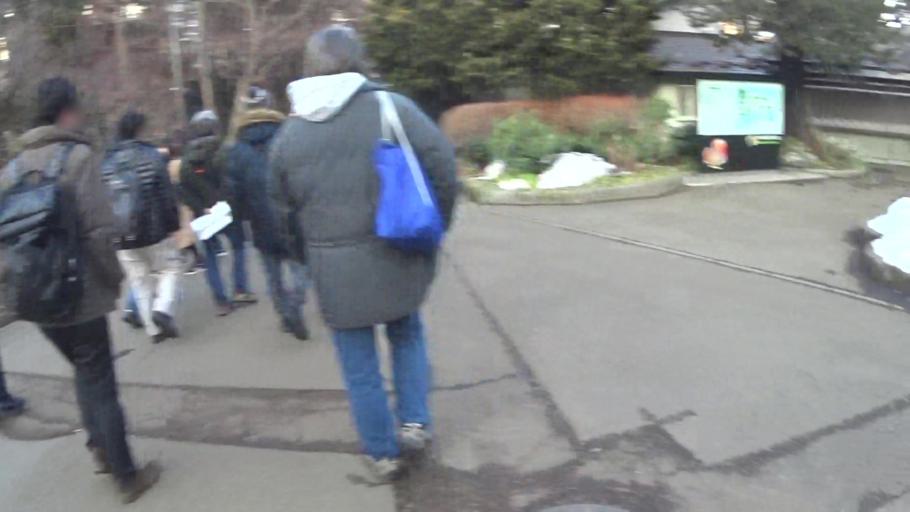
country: JP
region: Tokyo
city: Musashino
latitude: 35.7001
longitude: 139.5747
